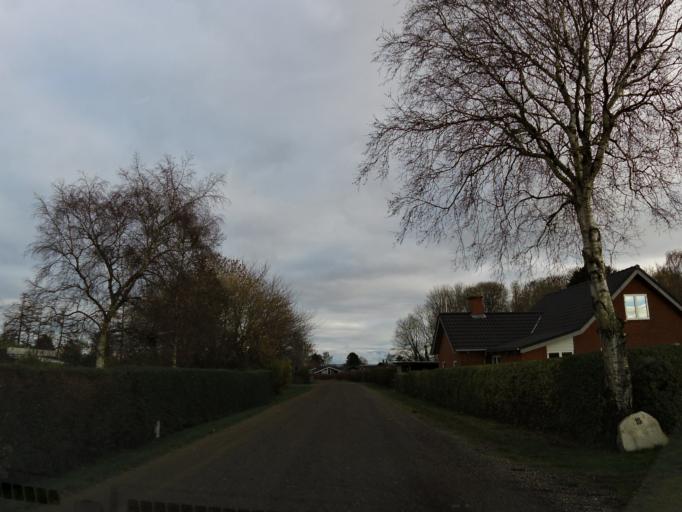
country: DK
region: Central Jutland
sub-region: Arhus Kommune
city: Malling
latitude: 55.9627
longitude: 10.2568
